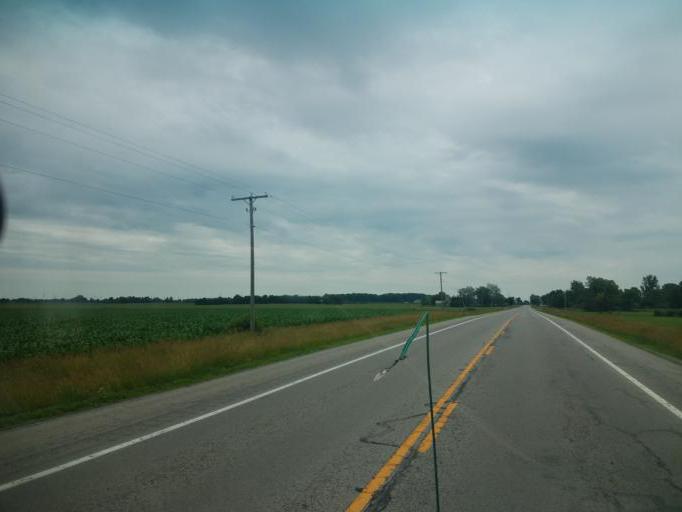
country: US
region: Ohio
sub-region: Hardin County
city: Ada
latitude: 40.7329
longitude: -83.8193
